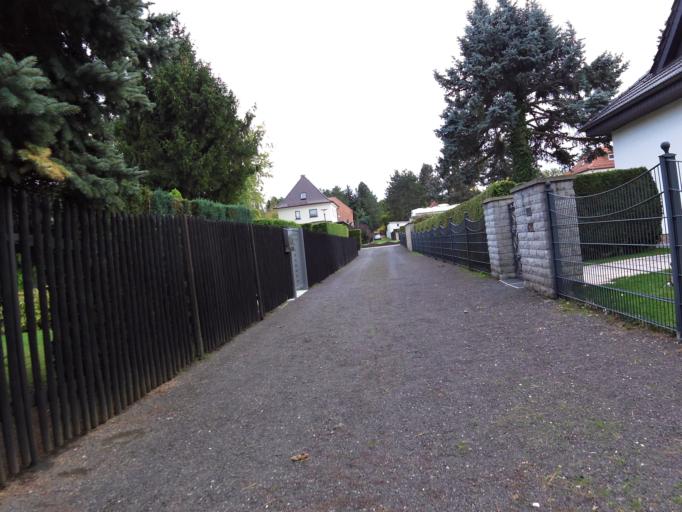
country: DE
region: Saxony
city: Grossposna
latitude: 51.2949
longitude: 12.4428
